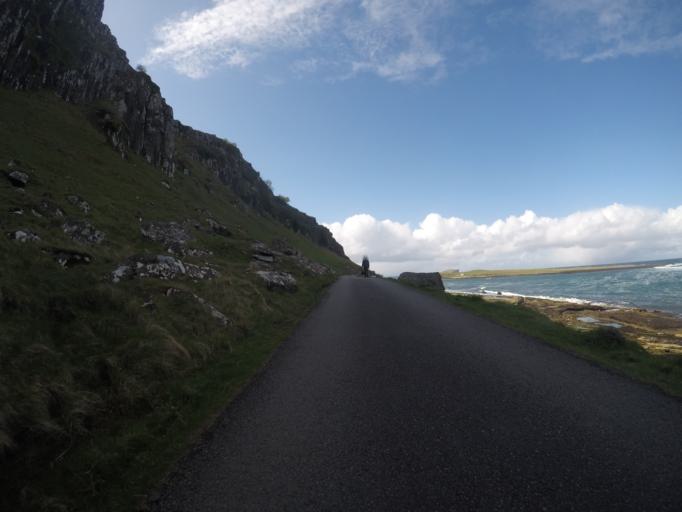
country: GB
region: Scotland
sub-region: Highland
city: Portree
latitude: 57.6342
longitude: -6.2019
